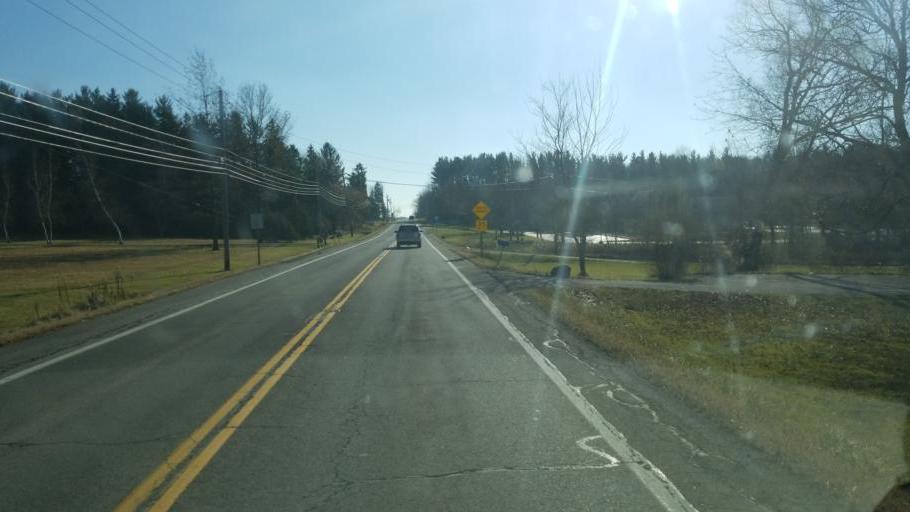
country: US
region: Ohio
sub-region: Geauga County
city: Burton
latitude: 41.5111
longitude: -81.1936
